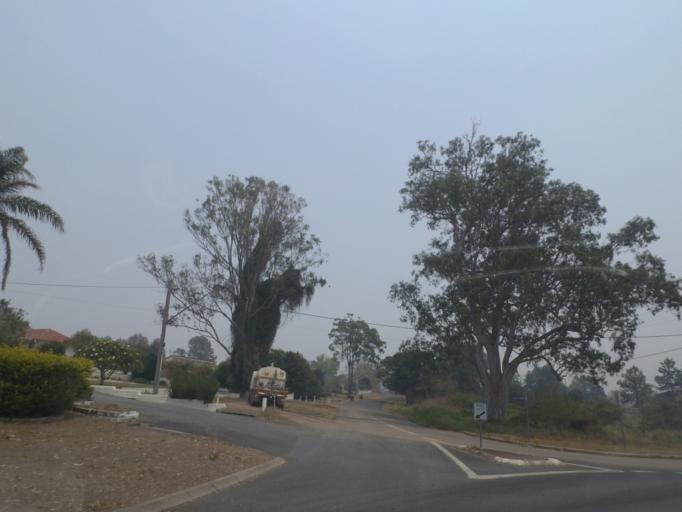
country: AU
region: New South Wales
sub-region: Clarence Valley
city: Maclean
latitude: -29.5653
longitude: 153.1434
